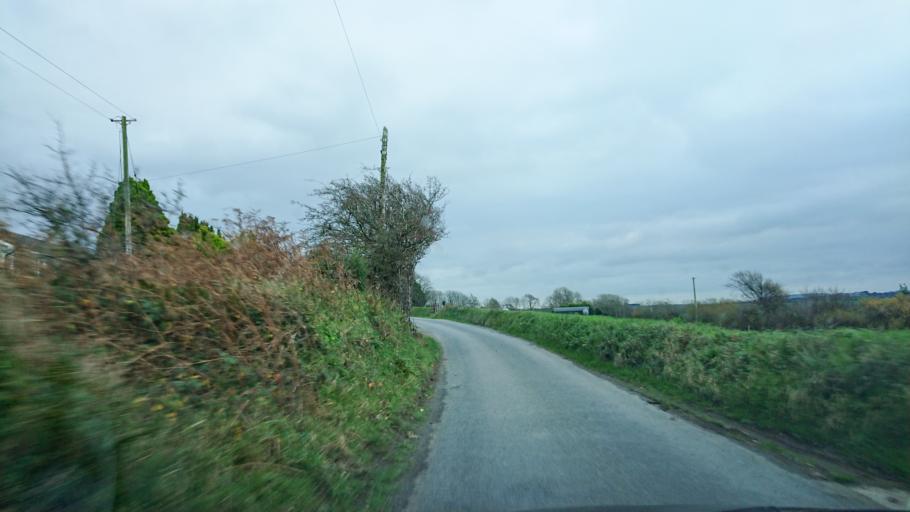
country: IE
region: Munster
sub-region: Waterford
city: Dunmore East
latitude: 52.2505
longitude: -7.0086
